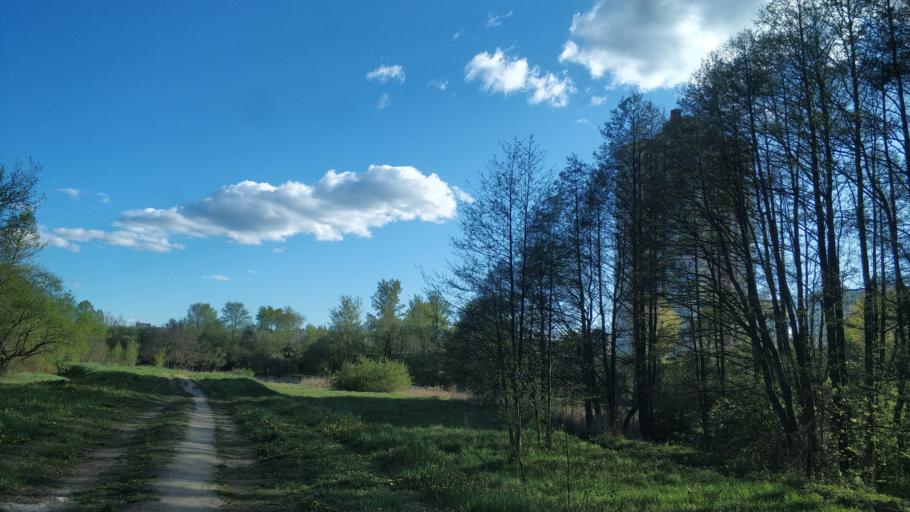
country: BY
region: Minsk
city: Minsk
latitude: 53.8666
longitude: 27.5778
